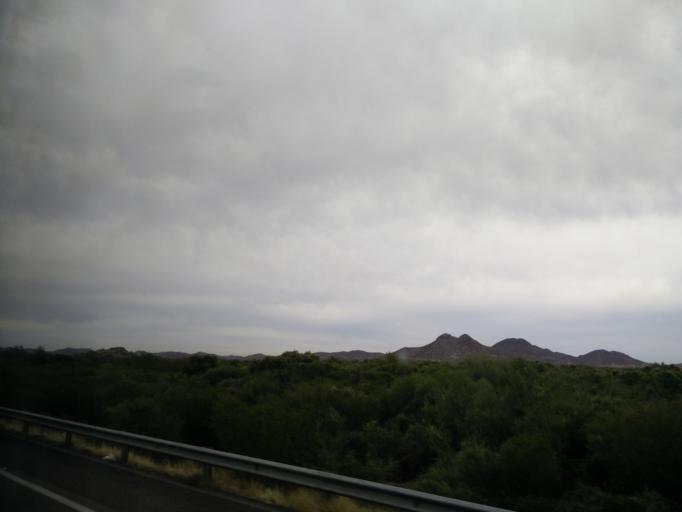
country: MX
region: Sonora
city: Hermosillo
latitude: 28.8673
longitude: -110.9585
